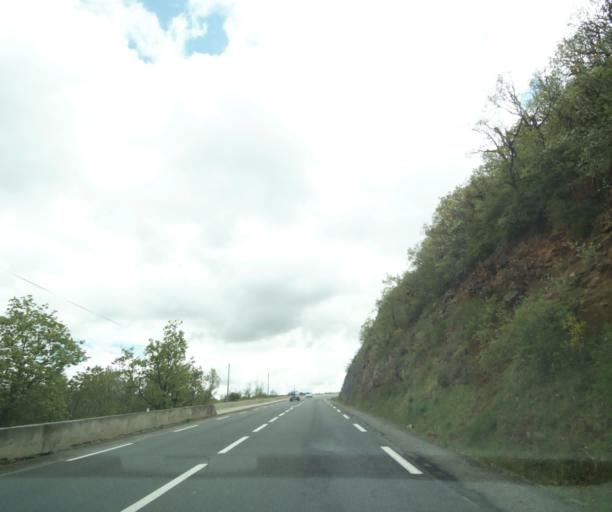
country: FR
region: Midi-Pyrenees
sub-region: Departement de l'Aveyron
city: Millau
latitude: 44.0884
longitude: 3.1254
